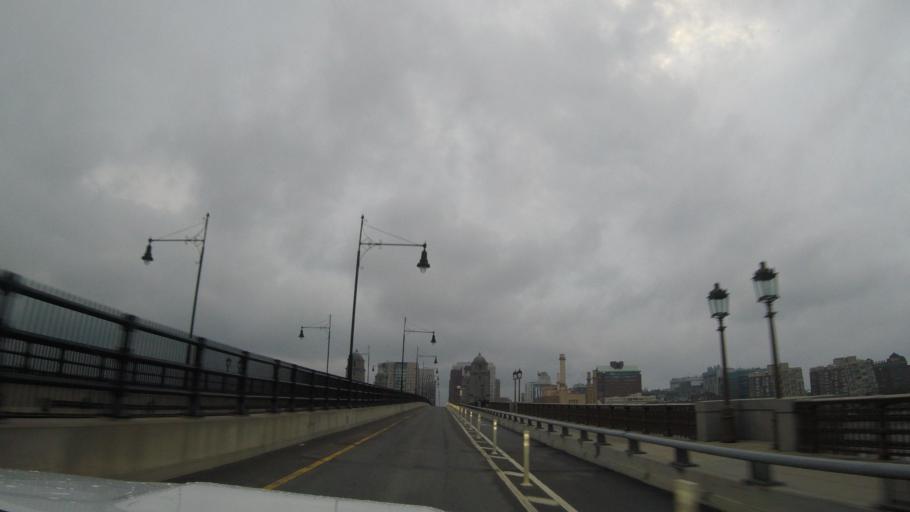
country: US
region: Massachusetts
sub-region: Suffolk County
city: Boston
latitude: 42.3608
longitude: -71.0733
